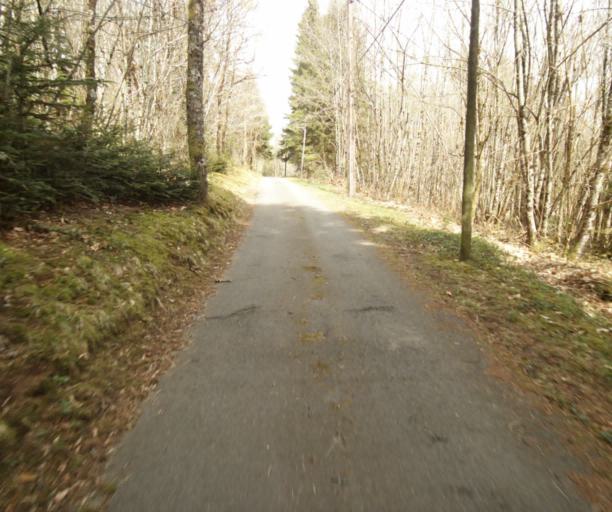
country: FR
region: Limousin
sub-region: Departement de la Correze
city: Argentat
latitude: 45.1902
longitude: 1.8870
